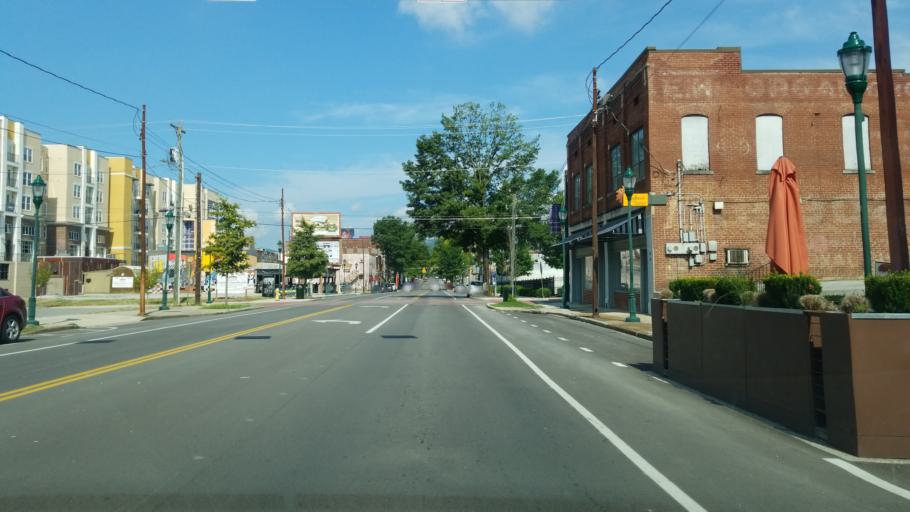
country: US
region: Tennessee
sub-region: Hamilton County
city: Chattanooga
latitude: 35.0431
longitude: -85.3011
